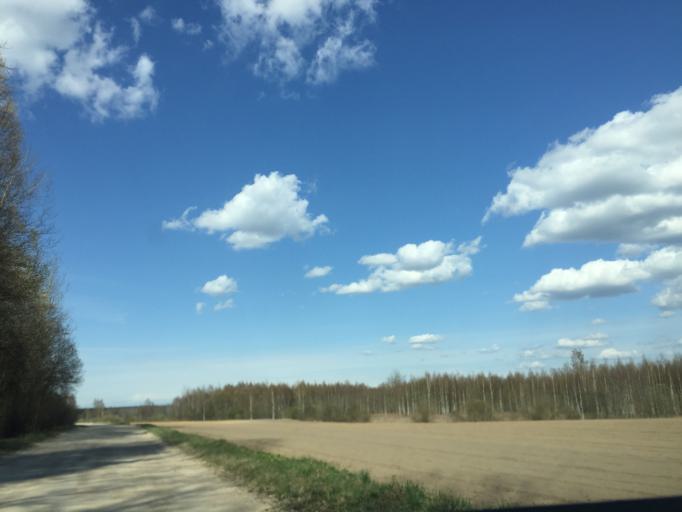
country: LV
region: Kegums
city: Kegums
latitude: 56.8253
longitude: 24.7927
